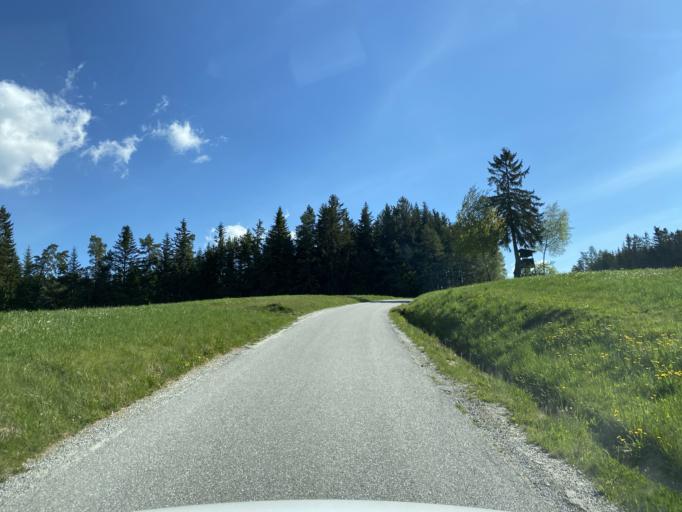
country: AT
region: Styria
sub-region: Politischer Bezirk Weiz
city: Strallegg
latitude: 47.3748
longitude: 15.7200
